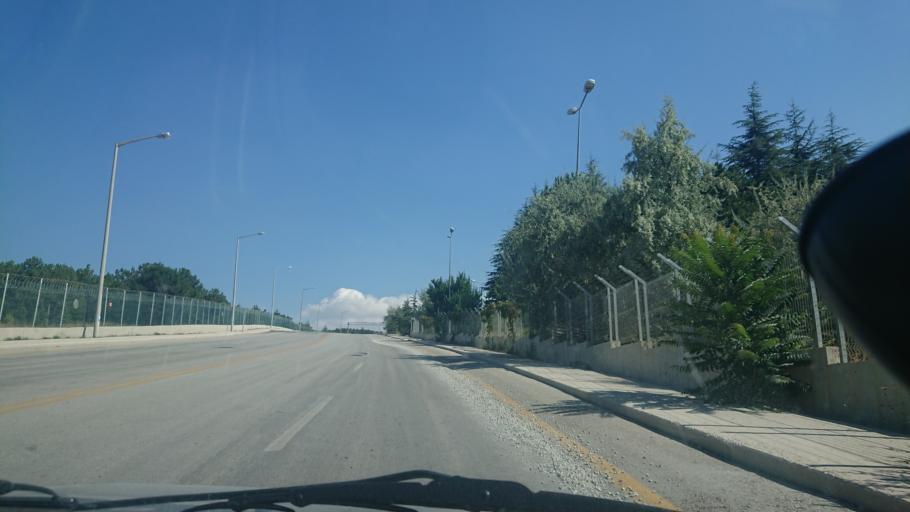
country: TR
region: Ankara
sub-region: Goelbasi
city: Golbasi
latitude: 39.8069
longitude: 32.8258
